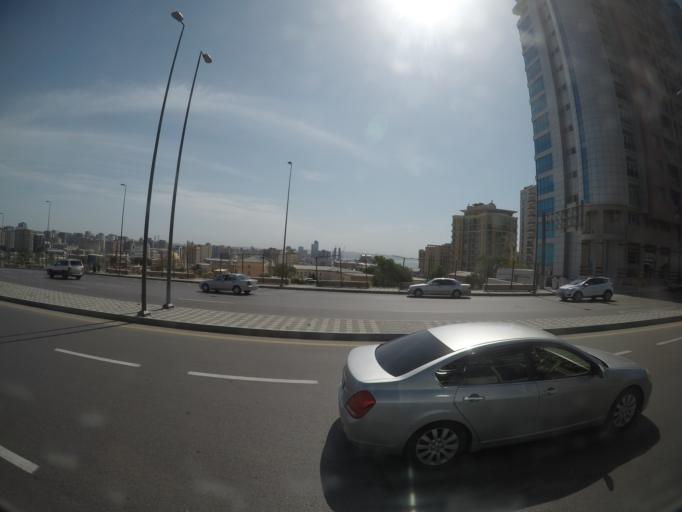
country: AZ
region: Baki
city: Badamdar
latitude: 40.3700
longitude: 49.8247
